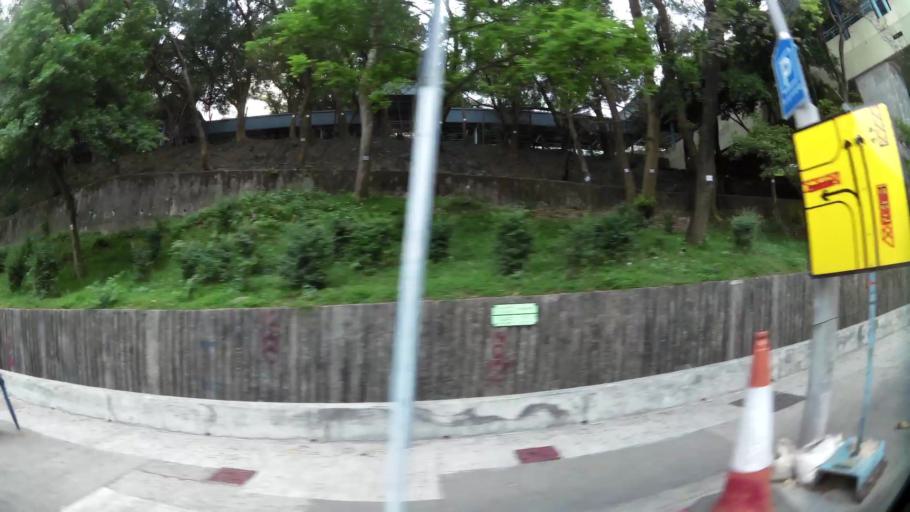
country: HK
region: Kowloon City
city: Kowloon
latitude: 22.3240
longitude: 114.2286
